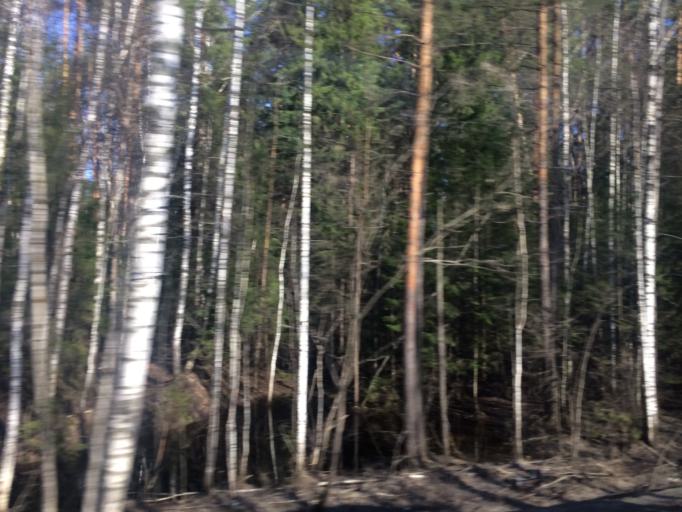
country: RU
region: Tatarstan
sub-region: Zelenodol'skiy Rayon
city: Vasil'yevo
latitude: 55.8935
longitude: 48.7283
